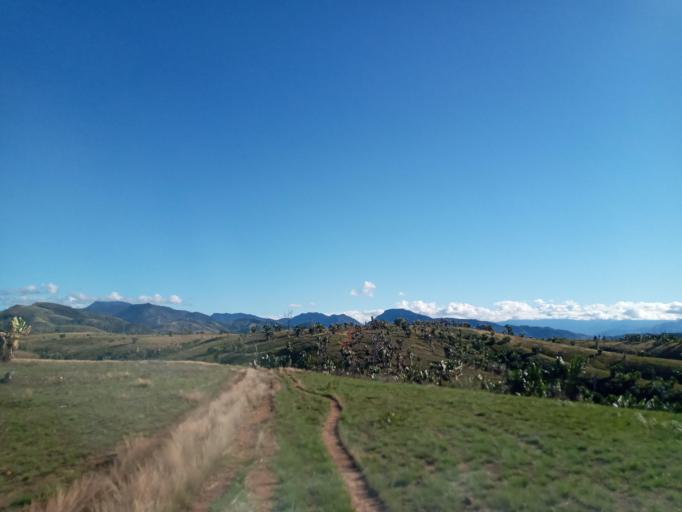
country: MG
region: Anosy
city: Fort Dauphin
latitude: -24.4061
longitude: 47.2488
